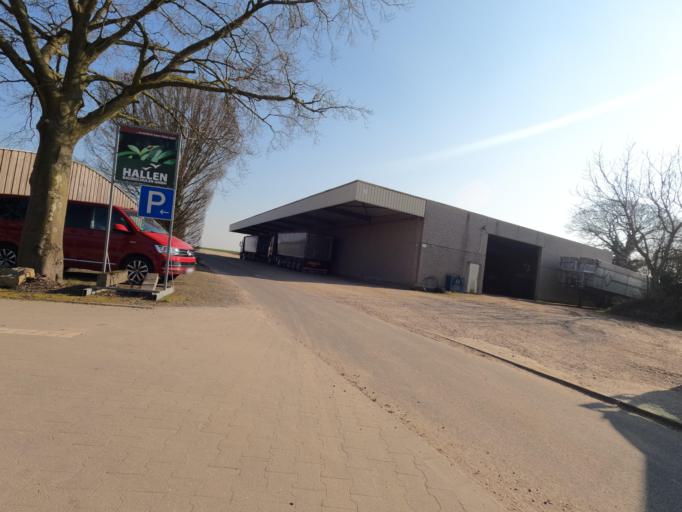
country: DE
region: North Rhine-Westphalia
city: Huckelhoven
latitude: 51.0831
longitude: 6.2543
